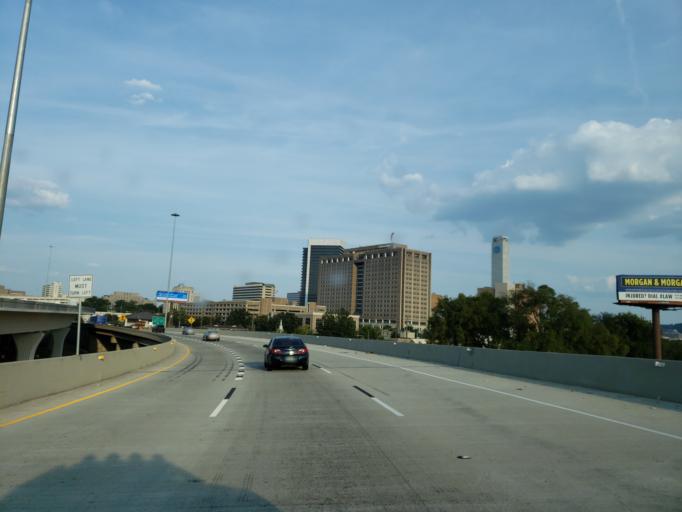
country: US
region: Alabama
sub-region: Jefferson County
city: Birmingham
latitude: 33.5194
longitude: -86.8184
